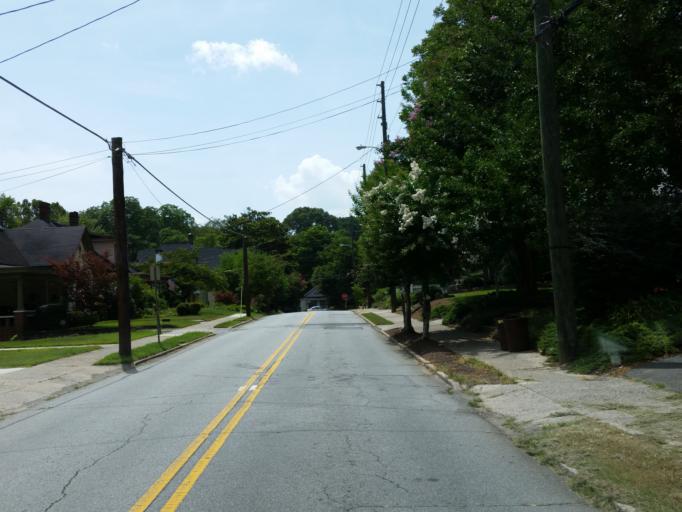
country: US
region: Georgia
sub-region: Cobb County
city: Marietta
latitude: 33.9609
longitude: -84.5508
